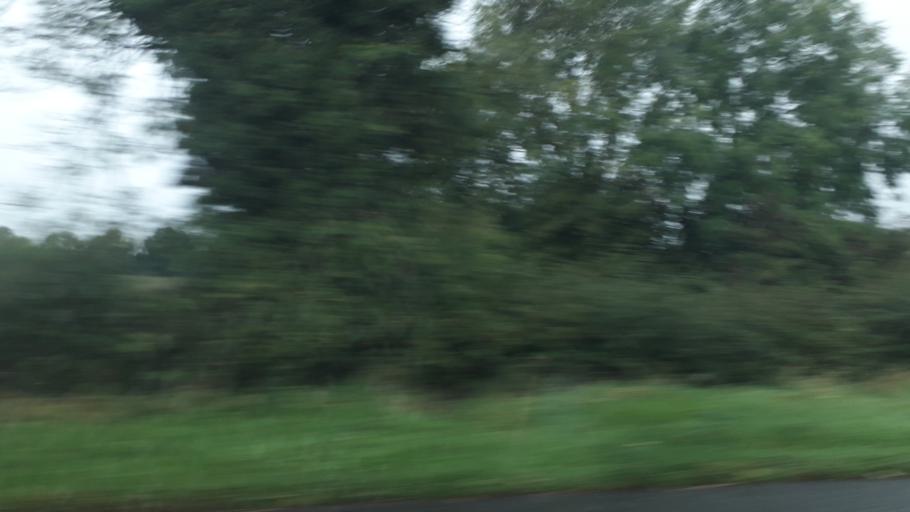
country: IE
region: Leinster
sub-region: An Iarmhi
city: An Muileann gCearr
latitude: 53.6185
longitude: -7.4535
